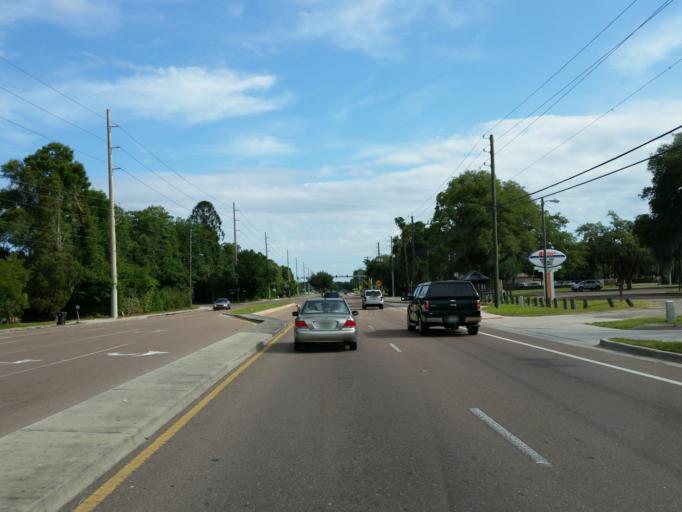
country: US
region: Florida
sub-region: Hillsborough County
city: Riverview
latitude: 27.8948
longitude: -82.3185
